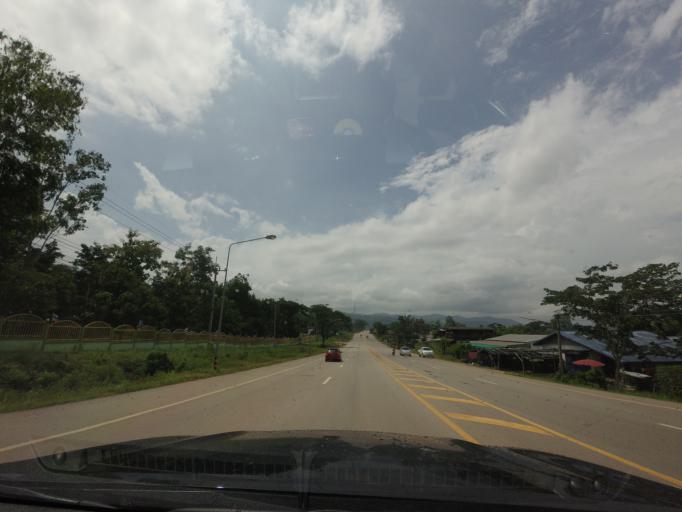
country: TH
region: Loei
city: Pak Chom
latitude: 18.0237
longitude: 101.8952
